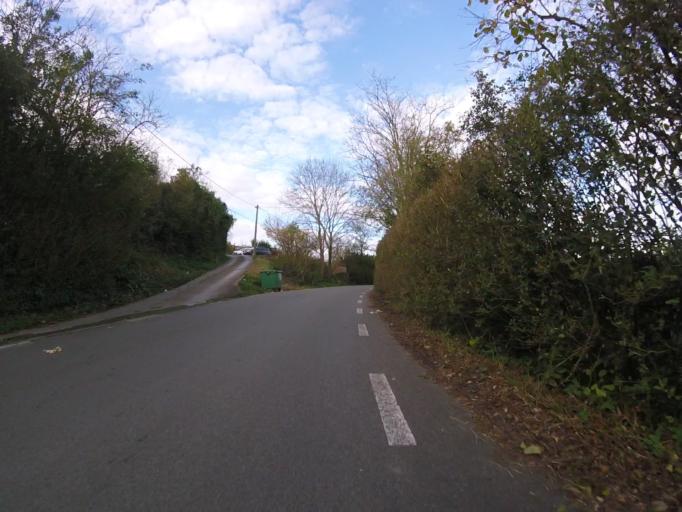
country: ES
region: Basque Country
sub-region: Provincia de Guipuzcoa
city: Errenteria
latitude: 43.3074
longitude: -1.9173
